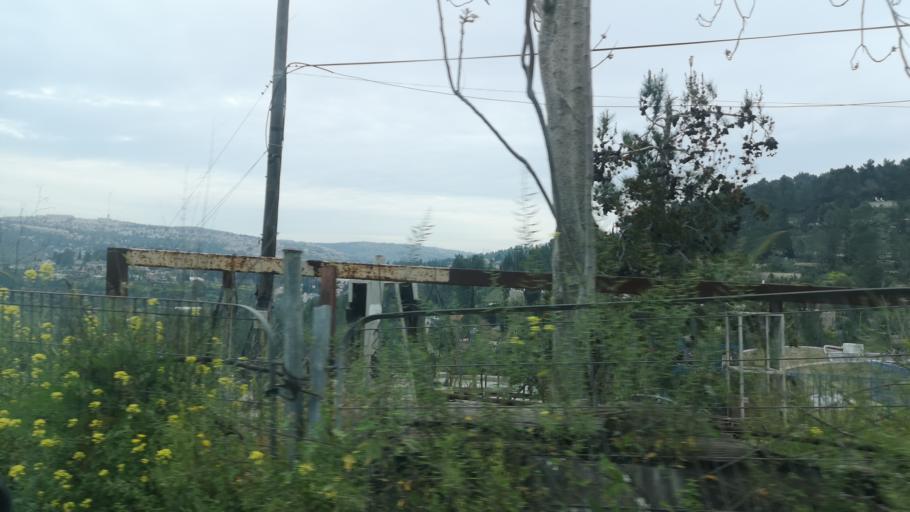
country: PS
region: West Bank
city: Bayt Iksa
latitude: 31.7700
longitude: 35.1607
